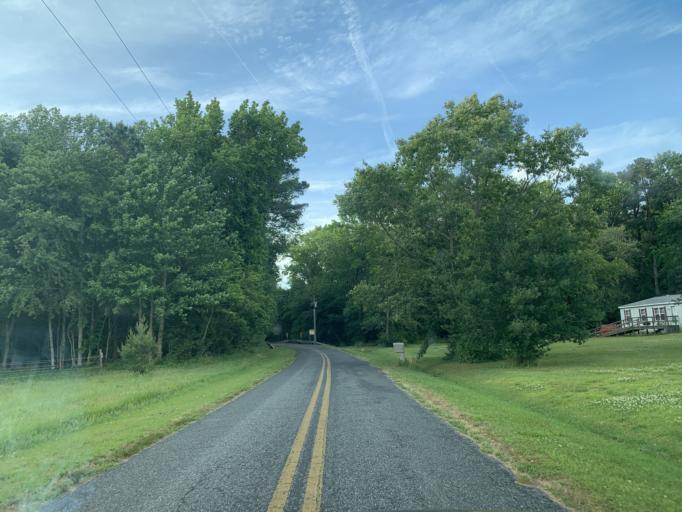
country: US
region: Maryland
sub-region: Worcester County
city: Pocomoke City
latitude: 38.0916
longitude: -75.4642
